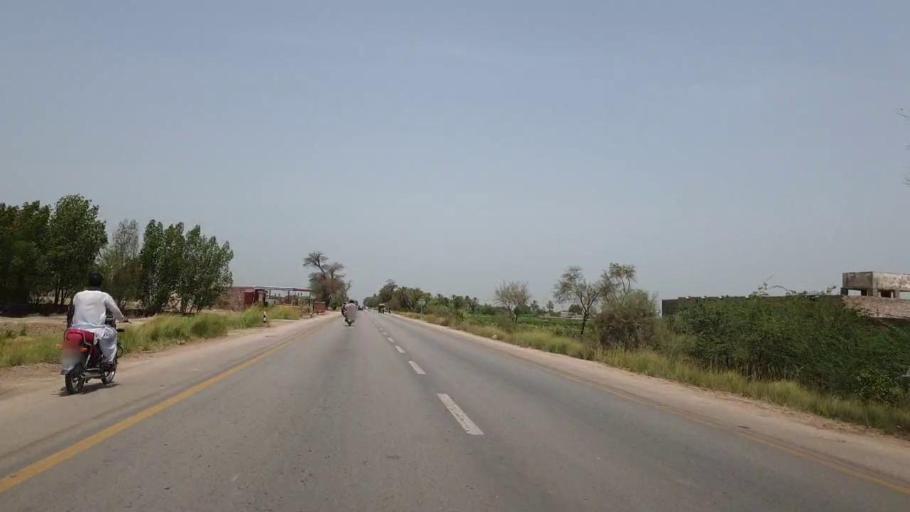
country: PK
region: Sindh
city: Nawabshah
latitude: 26.2162
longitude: 68.5064
